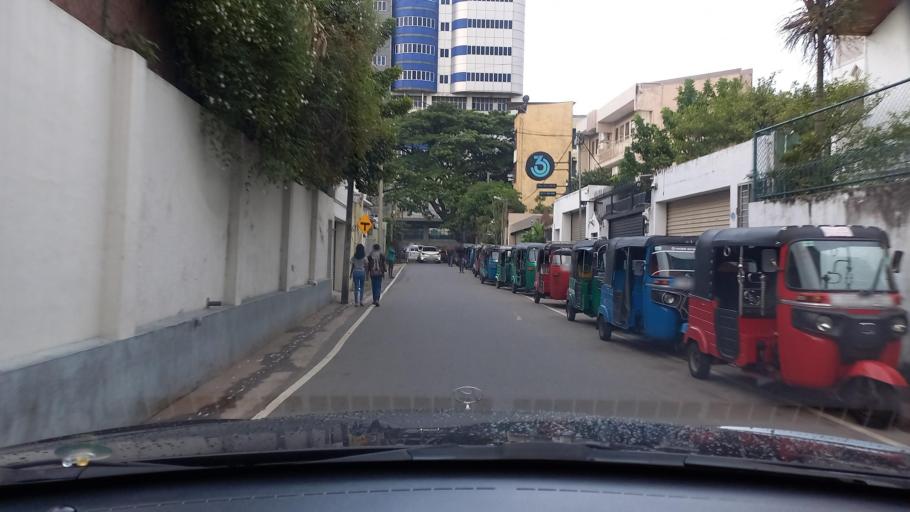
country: LK
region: Western
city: Pita Kotte
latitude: 6.8787
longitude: 79.8702
